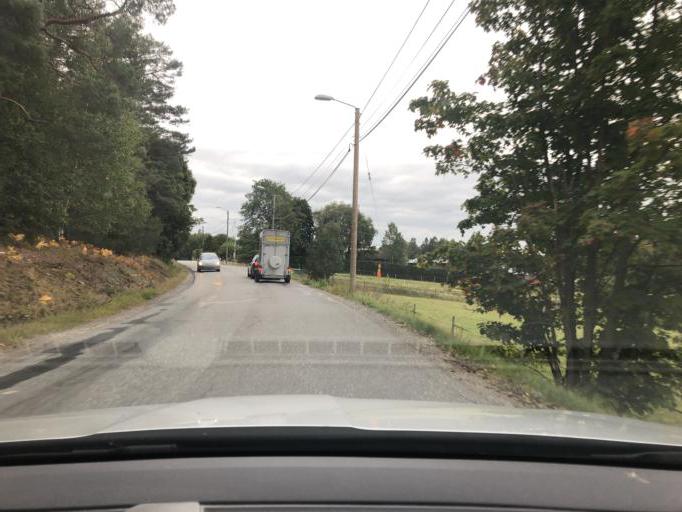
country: SE
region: Stockholm
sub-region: Haninge Kommun
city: Jordbro
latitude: 59.0970
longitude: 18.0364
